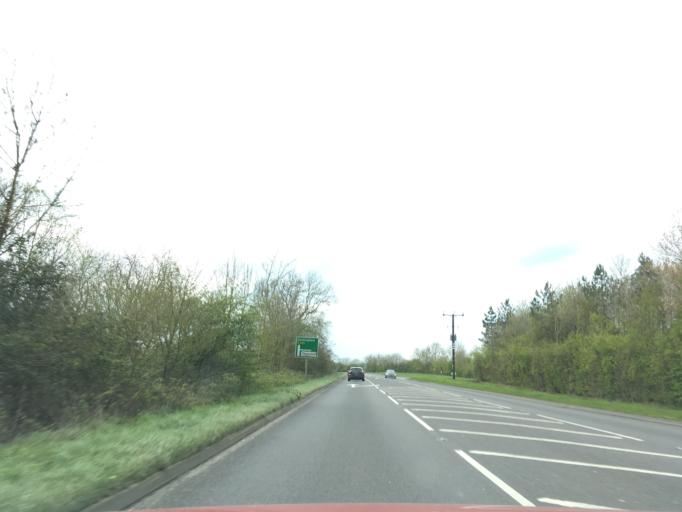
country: GB
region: England
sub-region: Buckinghamshire
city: Winslow
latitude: 51.9849
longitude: -0.8836
